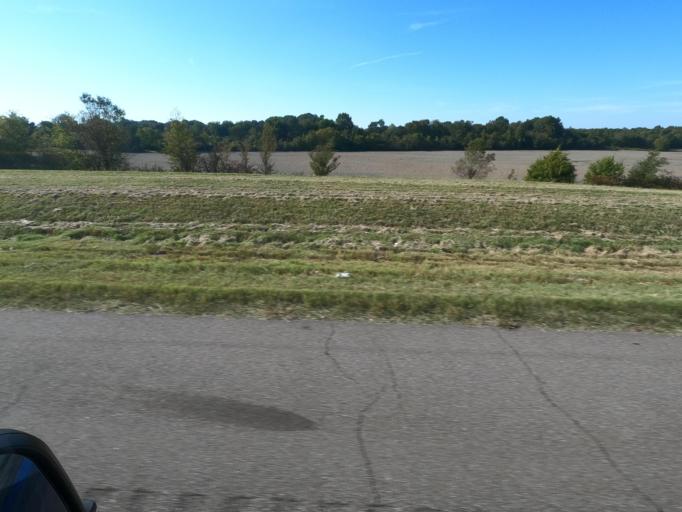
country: US
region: Tennessee
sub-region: Dyer County
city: Newbern
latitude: 36.1755
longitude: -89.2280
